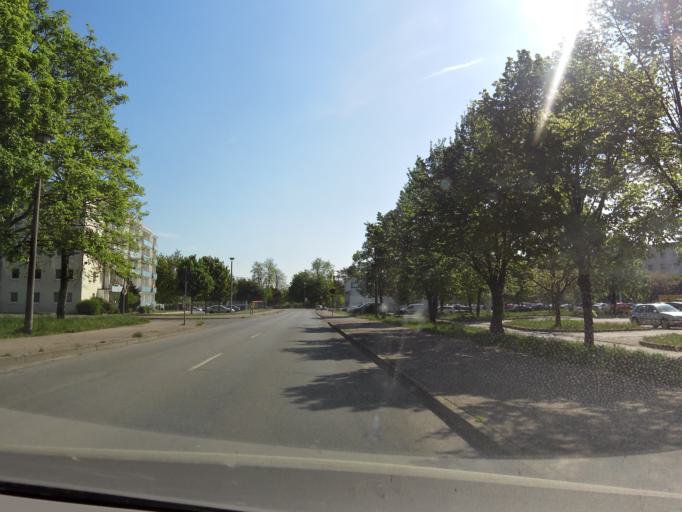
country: DE
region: Thuringia
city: Erfurt
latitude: 51.0142
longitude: 10.9934
